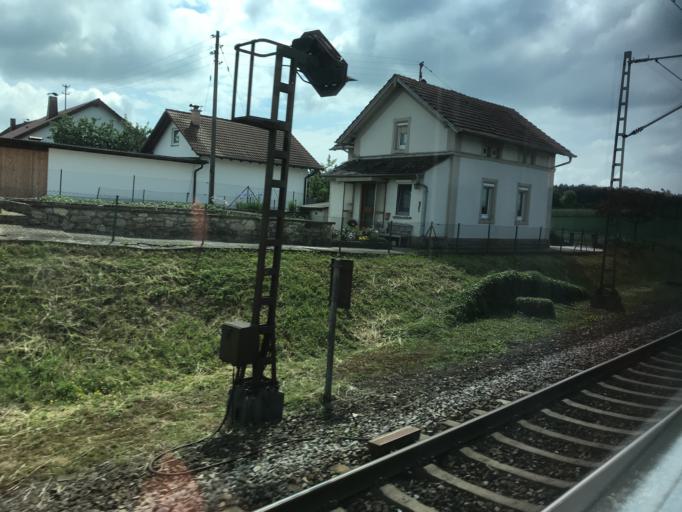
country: DE
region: Baden-Wuerttemberg
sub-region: Tuebingen Region
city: Westerstetten
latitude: 48.5073
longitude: 9.9501
